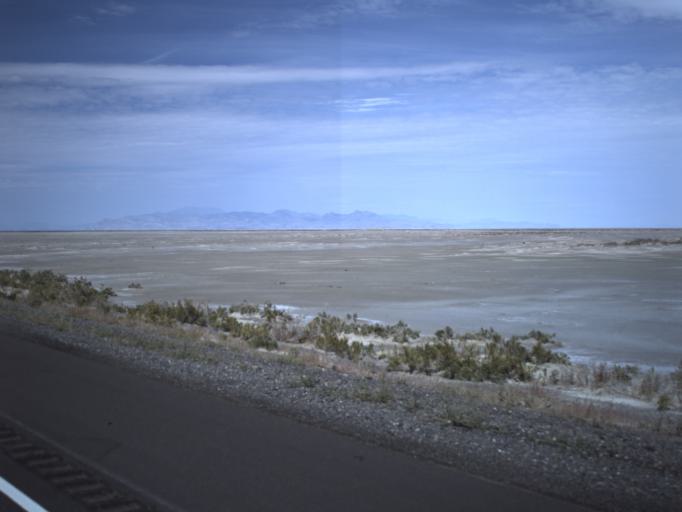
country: US
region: Utah
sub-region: Tooele County
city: Wendover
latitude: 40.7287
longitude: -113.3516
